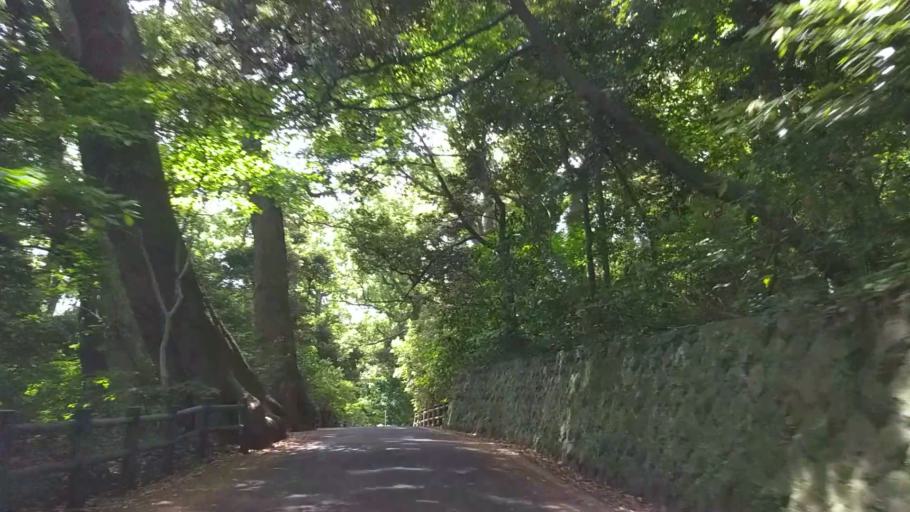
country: JP
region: Kanagawa
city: Yugawara
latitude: 35.1460
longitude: 139.1575
